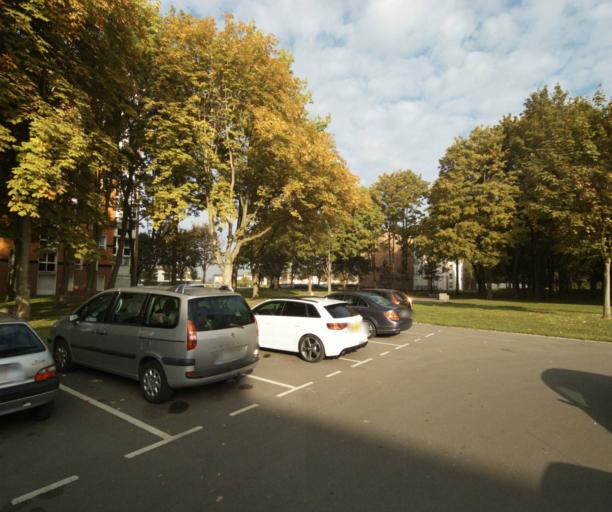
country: FR
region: Nord-Pas-de-Calais
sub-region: Departement du Nord
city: Wattignies
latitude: 50.5911
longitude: 3.0420
